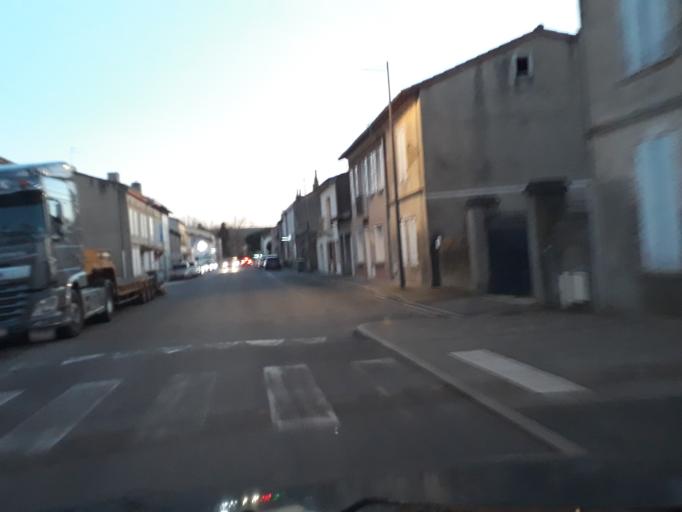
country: FR
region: Midi-Pyrenees
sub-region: Departement de la Haute-Garonne
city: Carbonne
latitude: 43.2993
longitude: 1.2250
